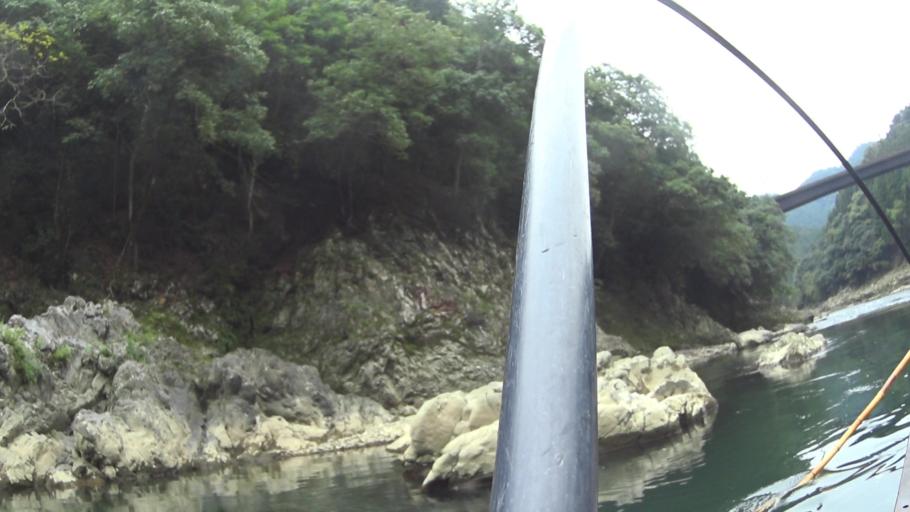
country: JP
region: Kyoto
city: Kameoka
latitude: 35.0242
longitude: 135.6315
